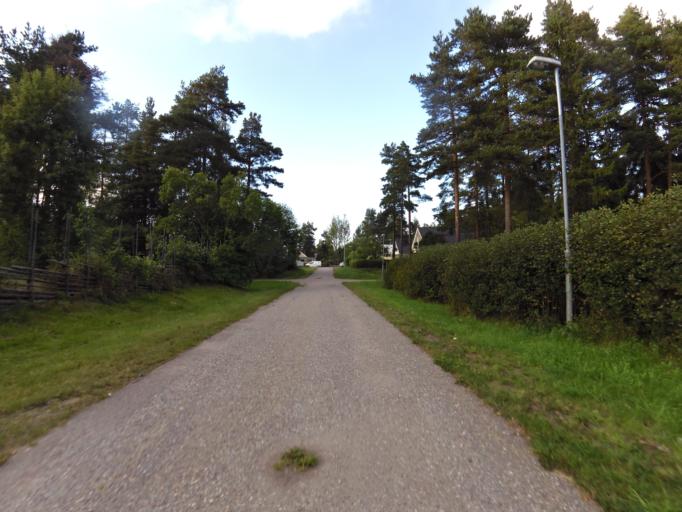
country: SE
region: Gaevleborg
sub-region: Gavle Kommun
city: Gavle
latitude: 60.6701
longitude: 17.2324
